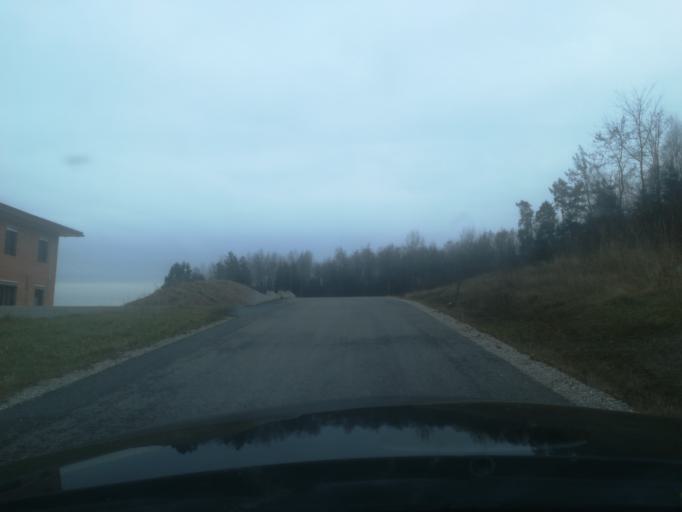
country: AT
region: Upper Austria
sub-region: Wels-Land
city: Neukirchen bei Lambach
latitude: 48.0986
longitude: 13.8119
